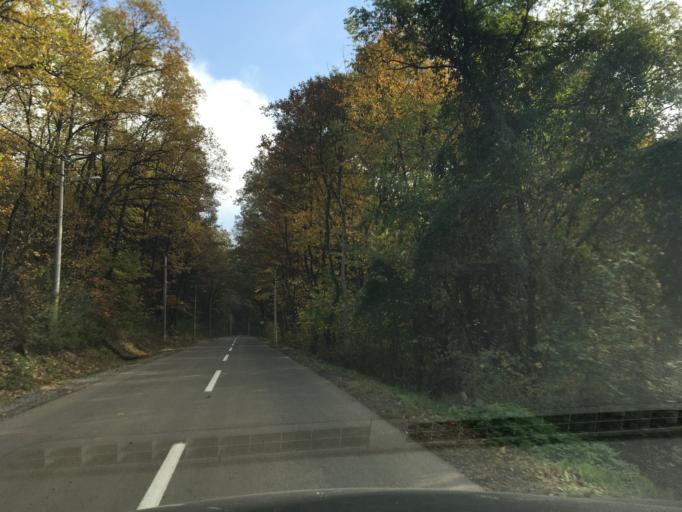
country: RS
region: Central Serbia
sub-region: Belgrade
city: Sopot
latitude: 44.4761
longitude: 20.5656
